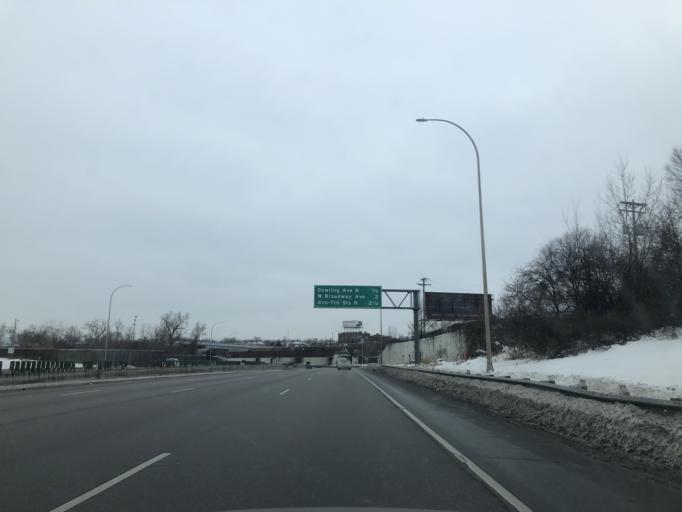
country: US
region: Minnesota
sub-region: Anoka County
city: Columbia Heights
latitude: 45.0351
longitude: -93.2868
